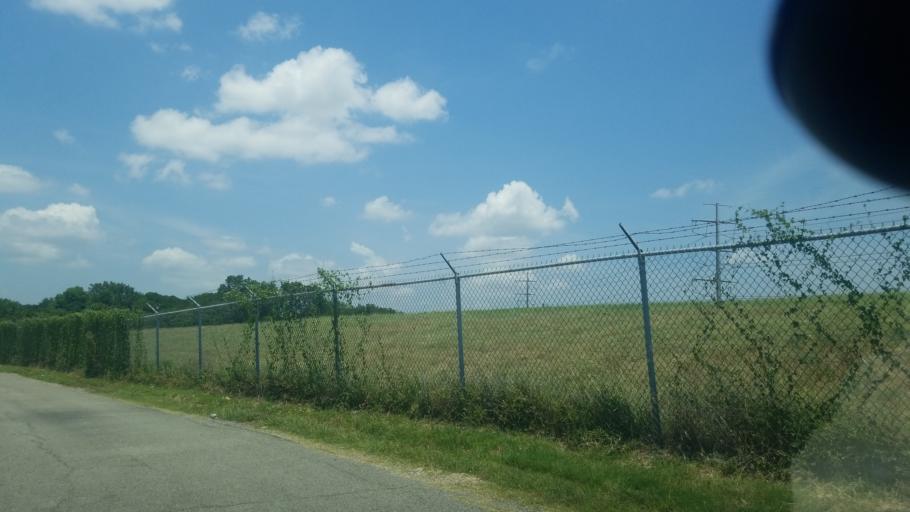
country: US
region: Texas
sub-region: Dallas County
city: Dallas
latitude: 32.7389
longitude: -96.7821
